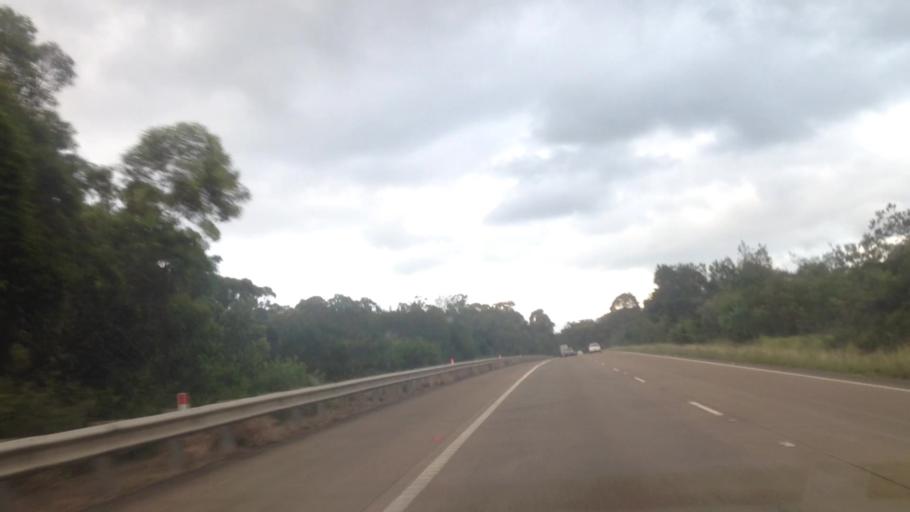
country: AU
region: New South Wales
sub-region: Lake Macquarie Shire
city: Dora Creek
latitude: -33.1497
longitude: 151.4733
